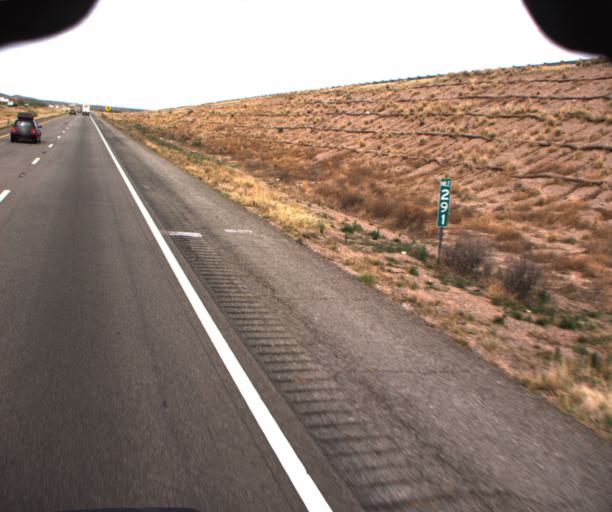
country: US
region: Arizona
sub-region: Cochise County
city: Mescal
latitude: 31.9822
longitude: -110.5369
